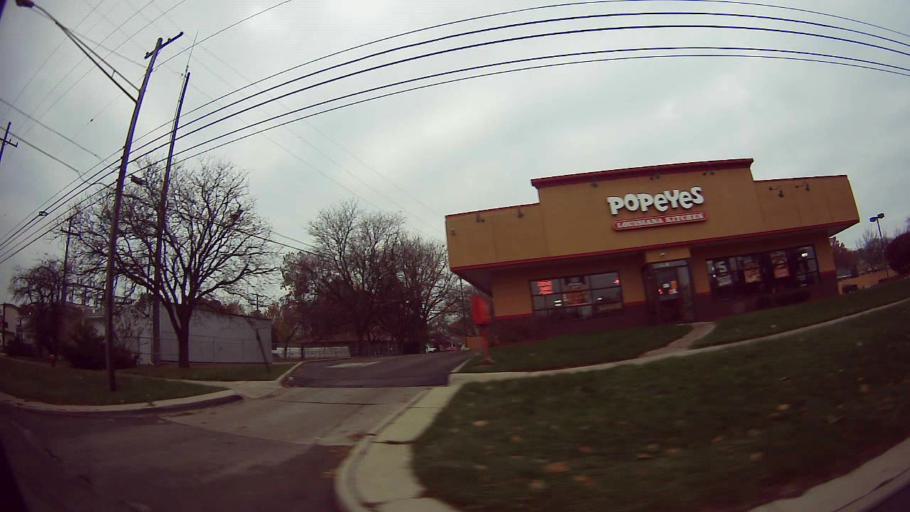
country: US
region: Michigan
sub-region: Wayne County
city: Redford
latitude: 42.3689
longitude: -83.2760
